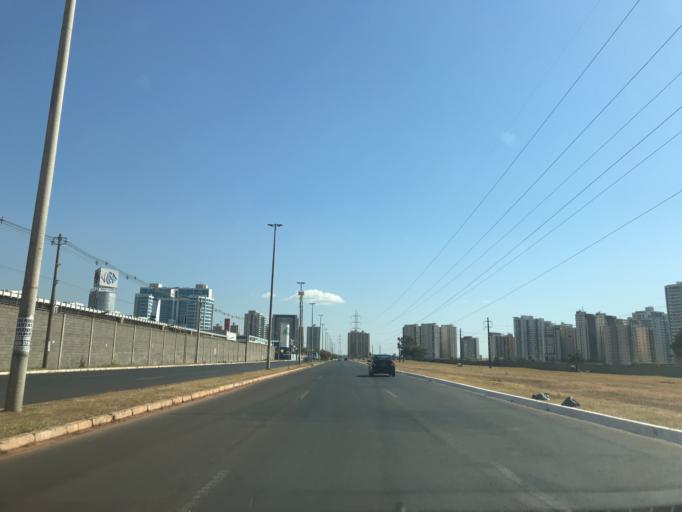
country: BR
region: Federal District
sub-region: Brasilia
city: Brasilia
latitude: -15.8460
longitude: -48.0399
